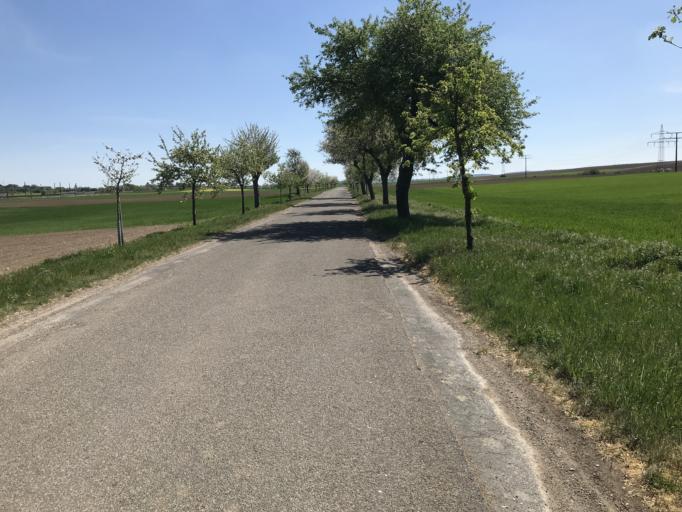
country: DE
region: Bavaria
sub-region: Regierungsbezirk Unterfranken
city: Iphofen
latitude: 49.6905
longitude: 10.2650
